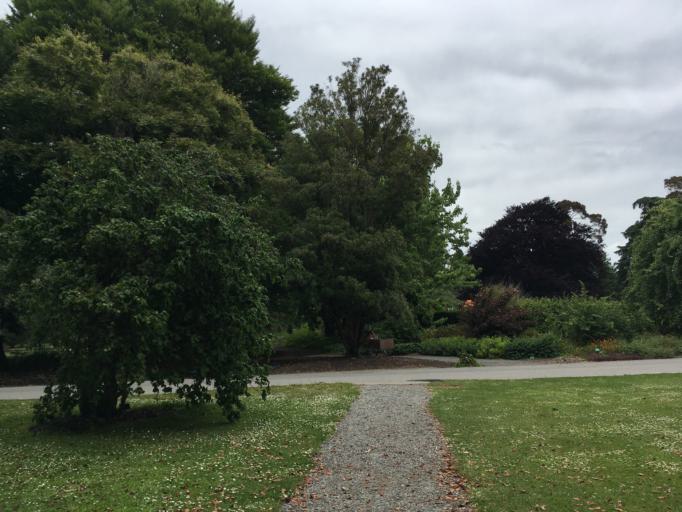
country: NZ
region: Canterbury
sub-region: Christchurch City
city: Christchurch
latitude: -43.5299
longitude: 172.6214
